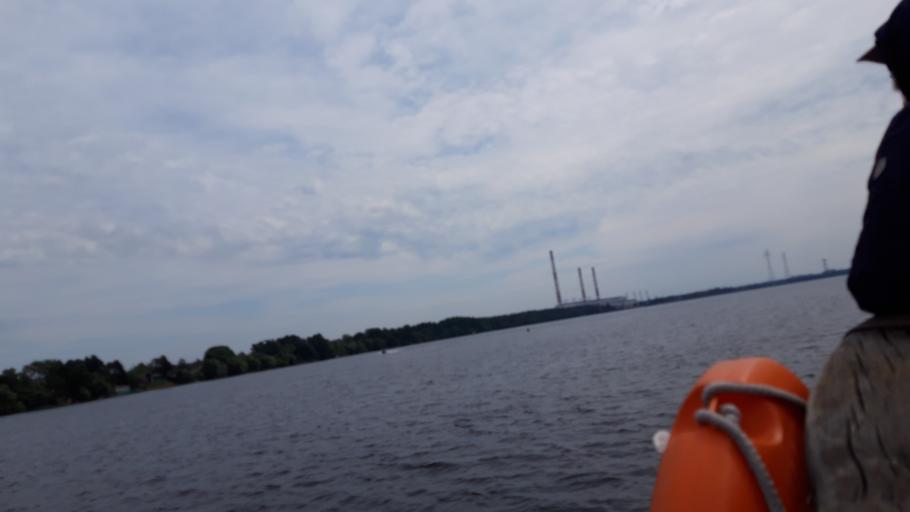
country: RU
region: Tverskaya
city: Konakovo
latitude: 56.7575
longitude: 36.7402
